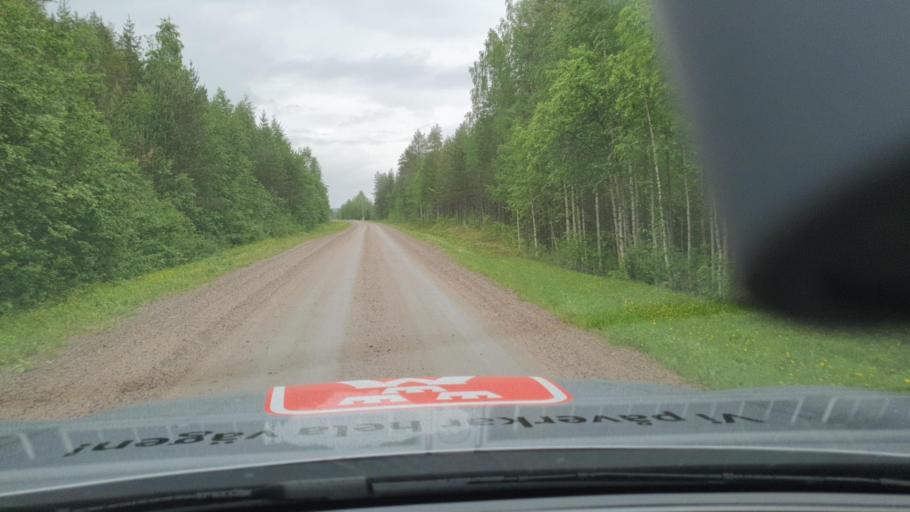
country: SE
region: Norrbotten
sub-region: Overkalix Kommun
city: OEverkalix
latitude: 66.5922
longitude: 22.7474
